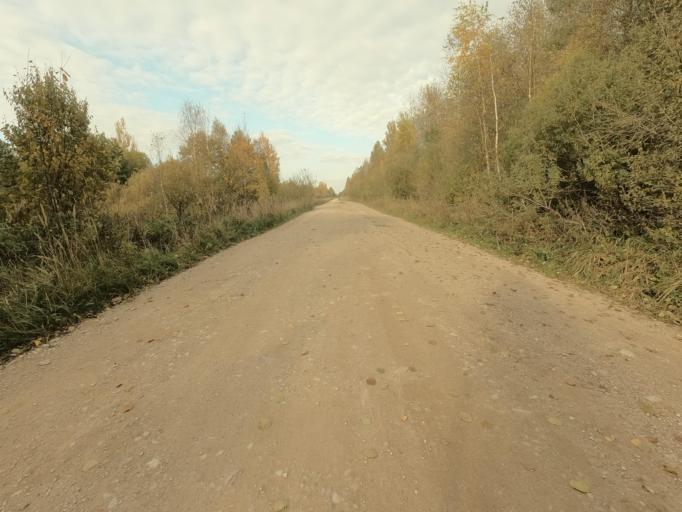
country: RU
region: Novgorod
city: Volkhovskiy
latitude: 58.9104
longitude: 31.0395
